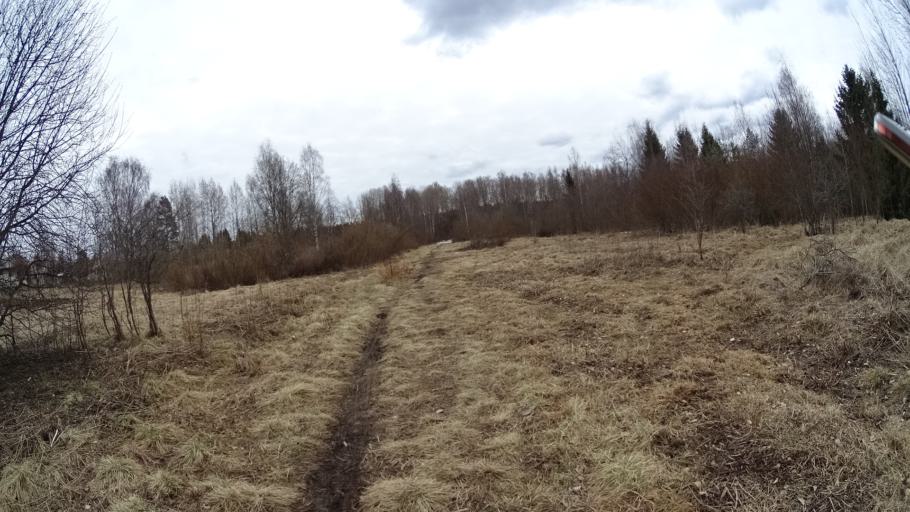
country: FI
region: Uusimaa
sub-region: Helsinki
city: Helsinki
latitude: 60.2750
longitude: 24.9067
